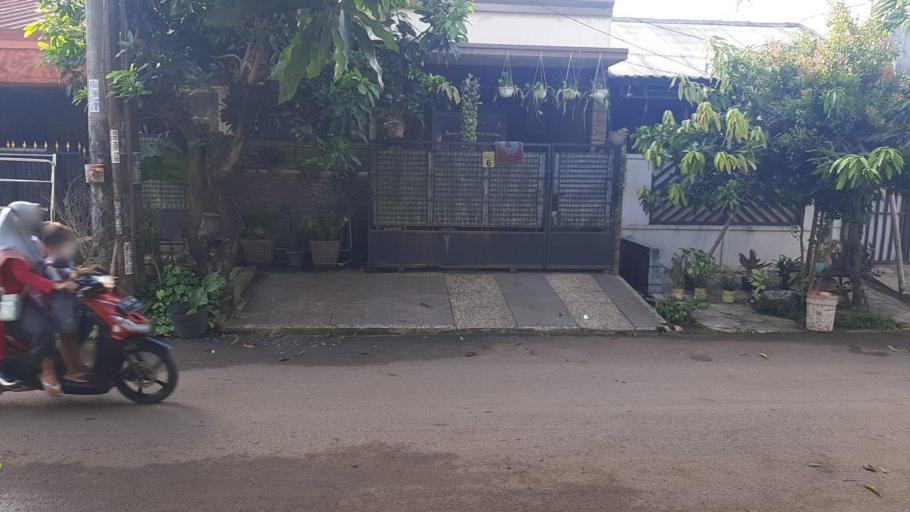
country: ID
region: West Java
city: Cileungsir
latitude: -6.3811
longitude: 107.0019
